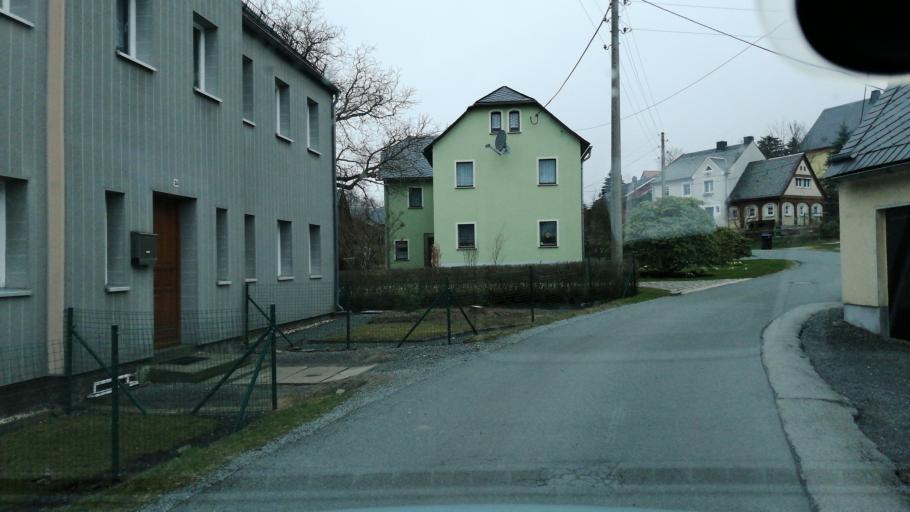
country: DE
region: Saxony
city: Schonbach
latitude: 51.0607
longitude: 14.5788
